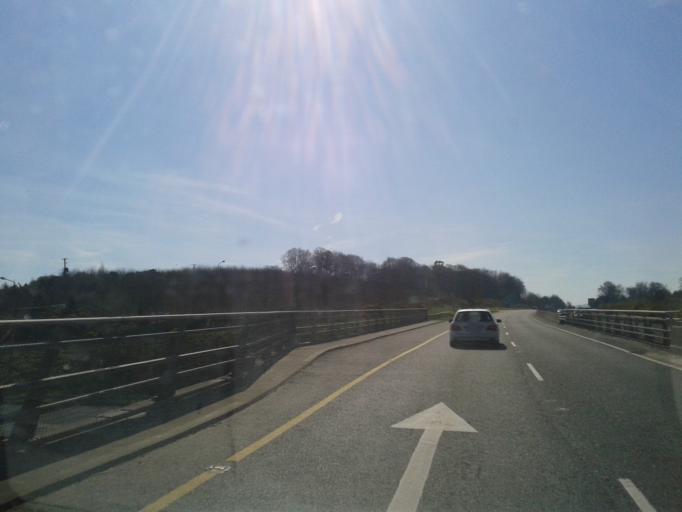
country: IE
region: Leinster
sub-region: Wicklow
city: Kilpedder
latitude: 53.1172
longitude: -6.1040
